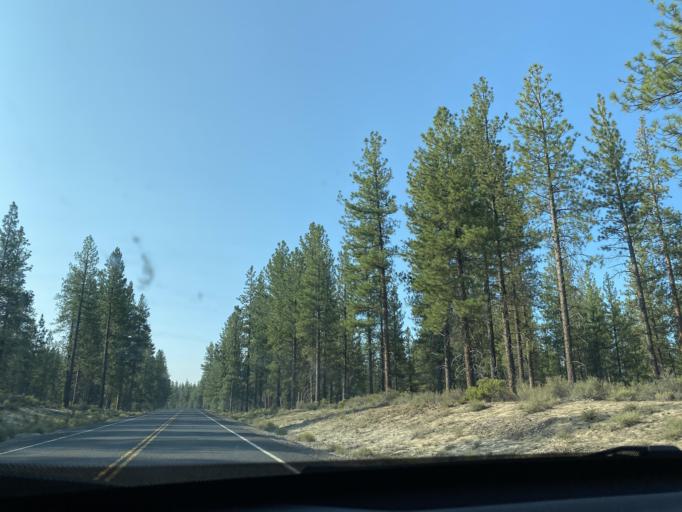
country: US
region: Oregon
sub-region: Deschutes County
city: La Pine
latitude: 43.7165
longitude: -121.4132
